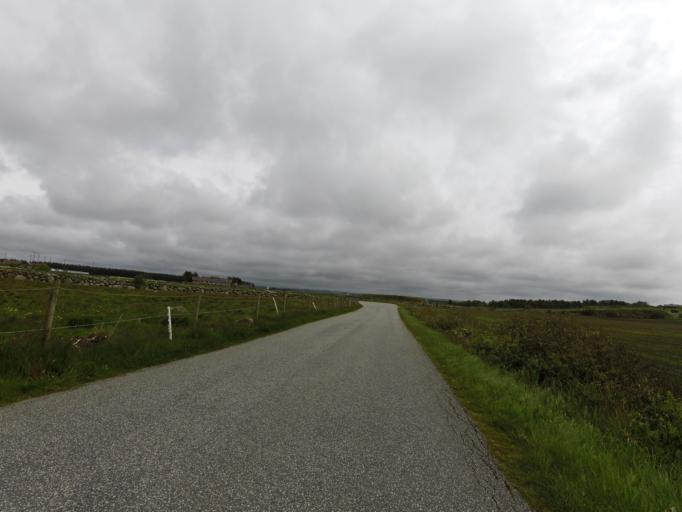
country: NO
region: Rogaland
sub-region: Ha
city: Naerbo
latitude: 58.6531
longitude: 5.5838
